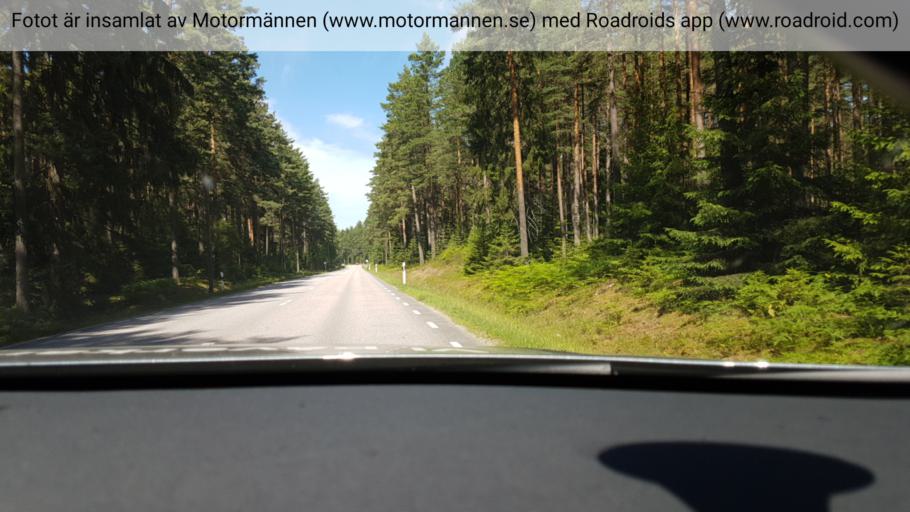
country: SE
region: Vaestra Goetaland
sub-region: Skovde Kommun
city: Stopen
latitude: 58.4609
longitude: 13.9571
